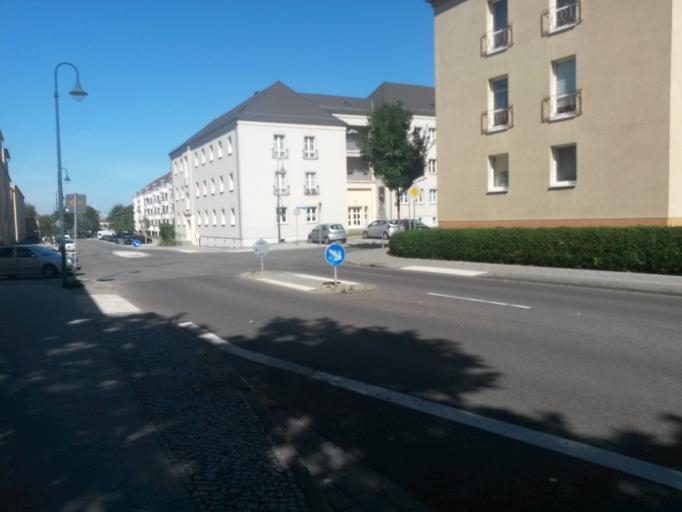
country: DE
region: Brandenburg
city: Prenzlau
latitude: 53.3150
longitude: 13.8577
